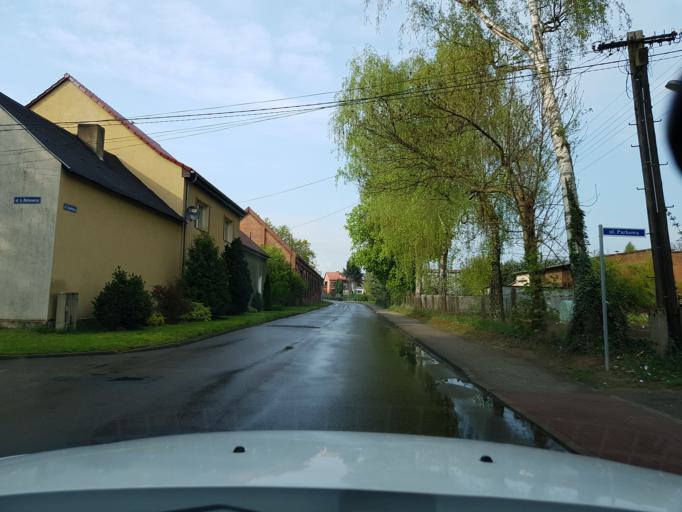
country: PL
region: West Pomeranian Voivodeship
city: Trzcinsko Zdroj
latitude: 52.9698
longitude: 14.6056
